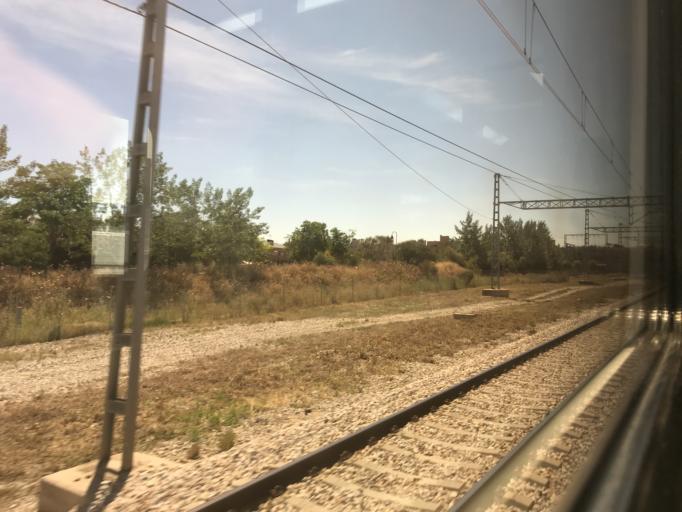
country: ES
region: Madrid
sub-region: Provincia de Madrid
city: Pinto
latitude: 40.2511
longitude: -3.7041
